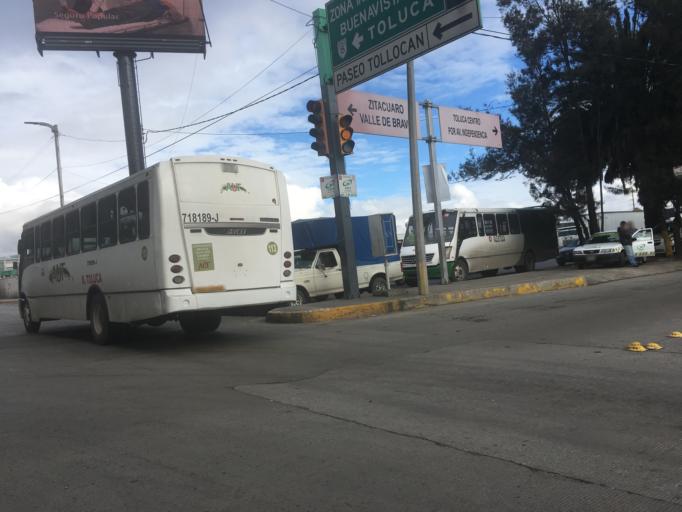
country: MX
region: Mexico
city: Santa Maria Totoltepec
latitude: 19.2882
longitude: -99.6103
